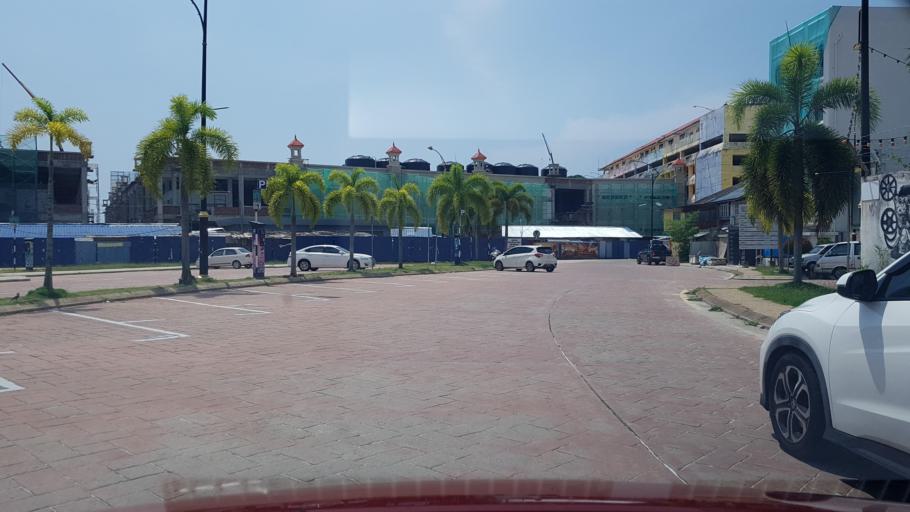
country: MY
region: Terengganu
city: Kuala Terengganu
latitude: 5.3354
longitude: 103.1342
